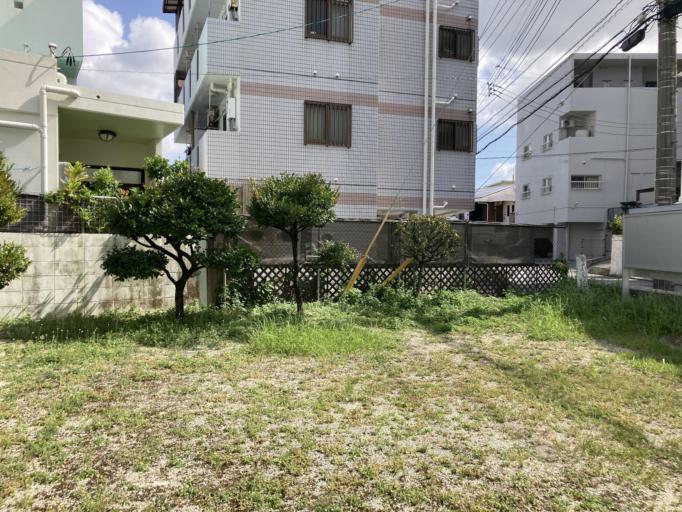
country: JP
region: Okinawa
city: Tomigusuku
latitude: 26.1976
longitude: 127.6750
